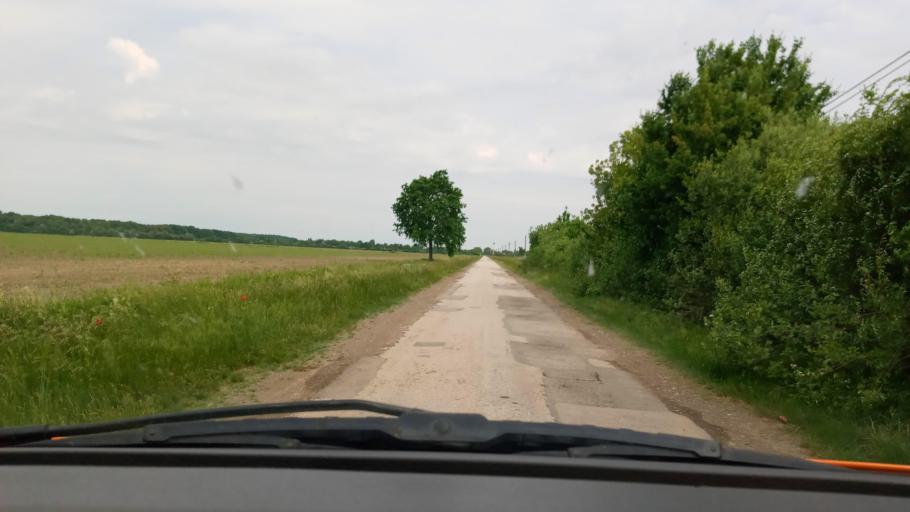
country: HU
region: Baranya
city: Vajszlo
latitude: 45.9140
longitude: 18.0266
